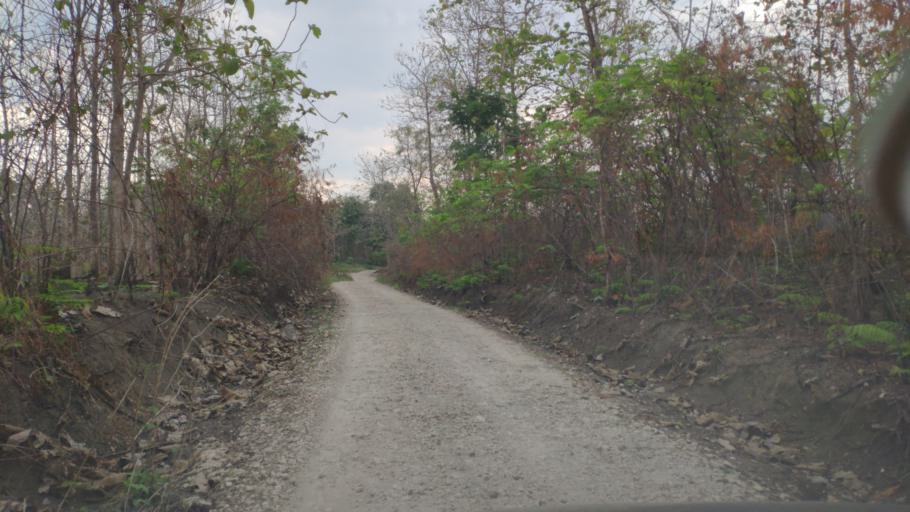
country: ID
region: Central Java
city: Randublatung
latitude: -7.2759
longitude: 111.2864
